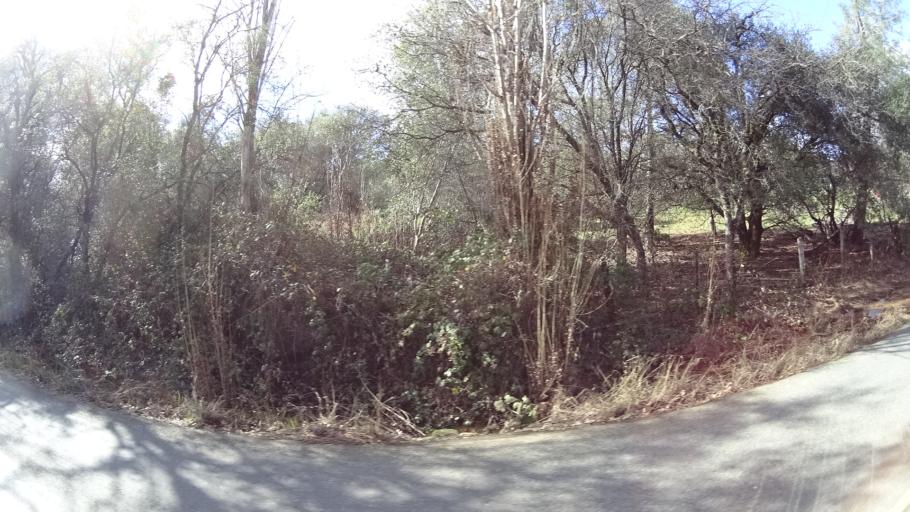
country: US
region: California
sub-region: Butte County
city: Berry Creek
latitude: 39.6407
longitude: -121.5289
